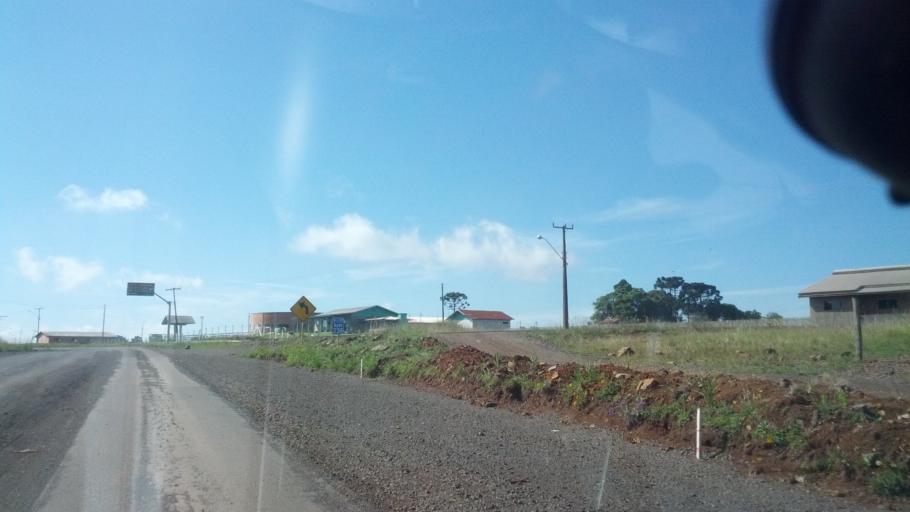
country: BR
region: Santa Catarina
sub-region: Lages
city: Lages
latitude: -27.9430
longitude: -50.5088
